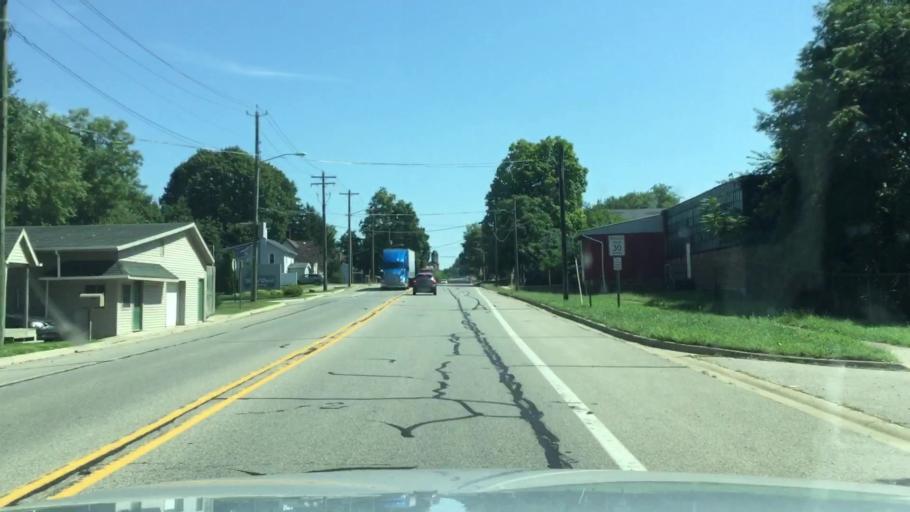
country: US
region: Michigan
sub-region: Lenawee County
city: Clinton
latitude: 42.0718
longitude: -83.9783
